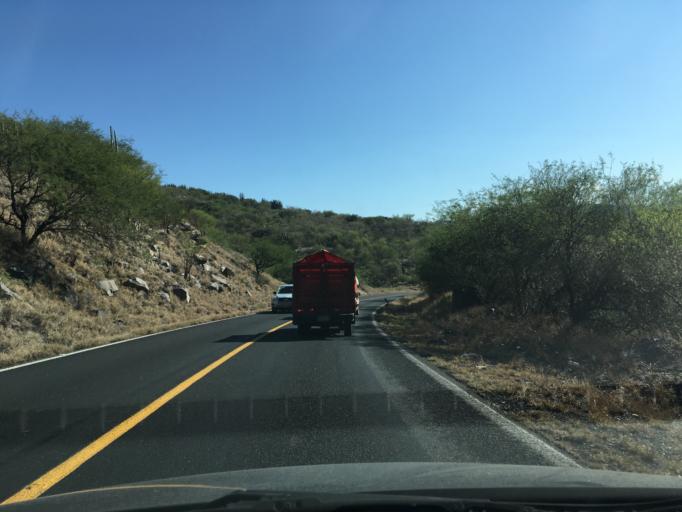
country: MX
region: Hidalgo
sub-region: San Agustin Metzquititlan
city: Mezquititlan
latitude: 20.4603
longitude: -98.6792
